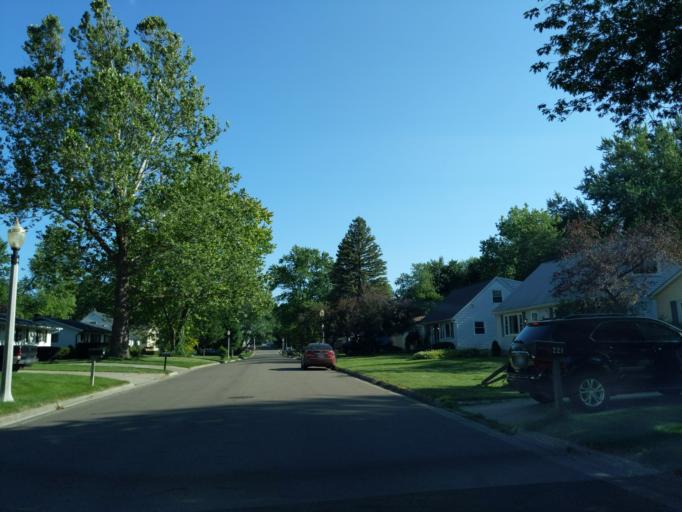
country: US
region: Michigan
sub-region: Eaton County
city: Waverly
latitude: 42.7358
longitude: -84.6182
